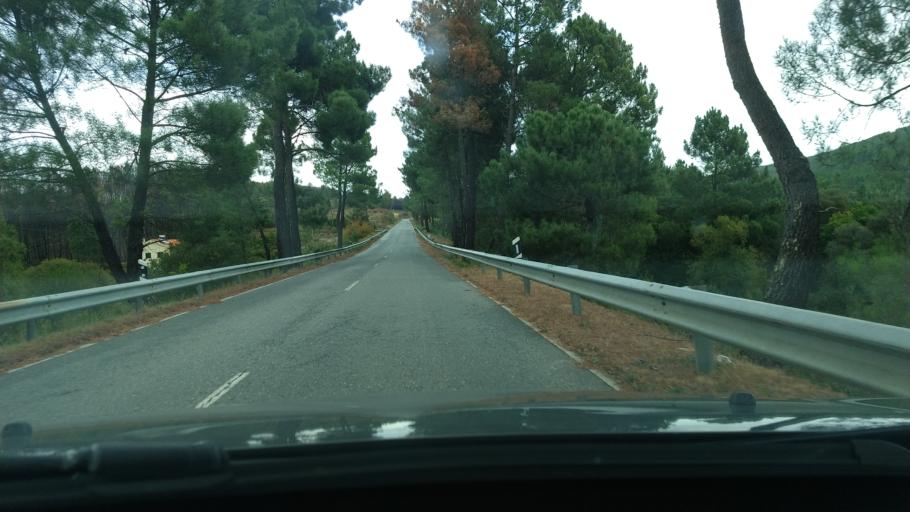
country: PT
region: Castelo Branco
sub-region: Covilha
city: Covilha
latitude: 40.2381
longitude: -7.5840
